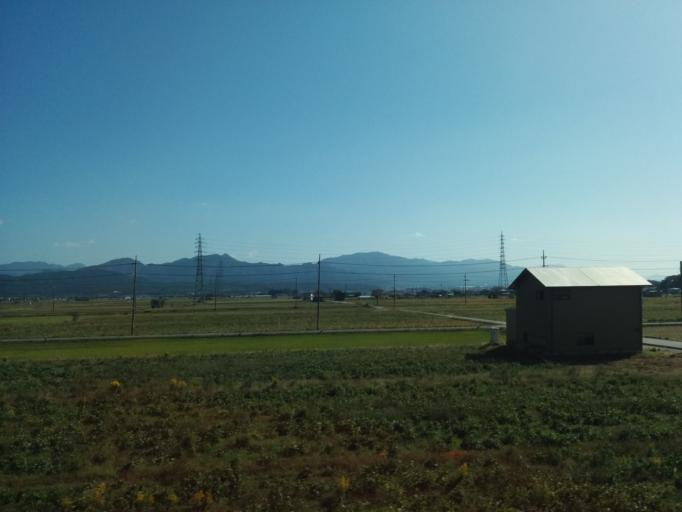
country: JP
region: Shiga Prefecture
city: Hikone
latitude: 35.2019
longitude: 136.2351
